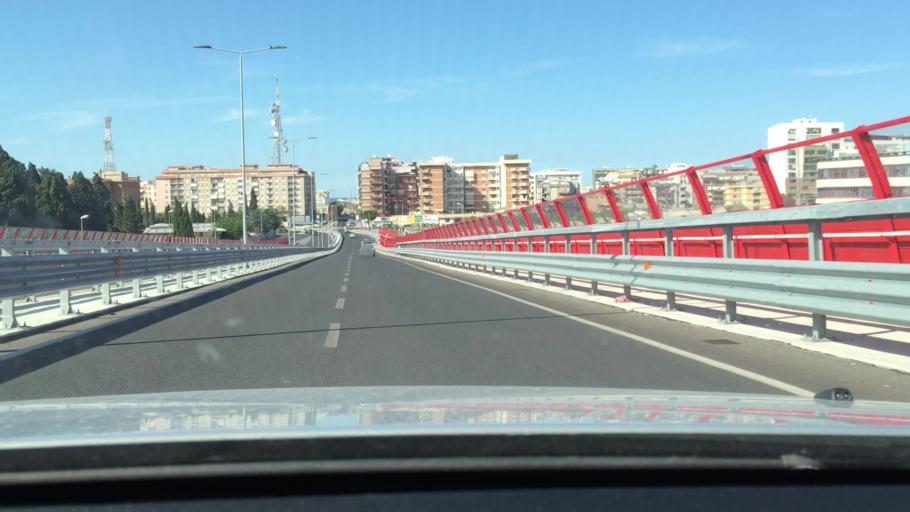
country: IT
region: Apulia
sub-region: Provincia di Bari
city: Bari
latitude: 41.1217
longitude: 16.8482
